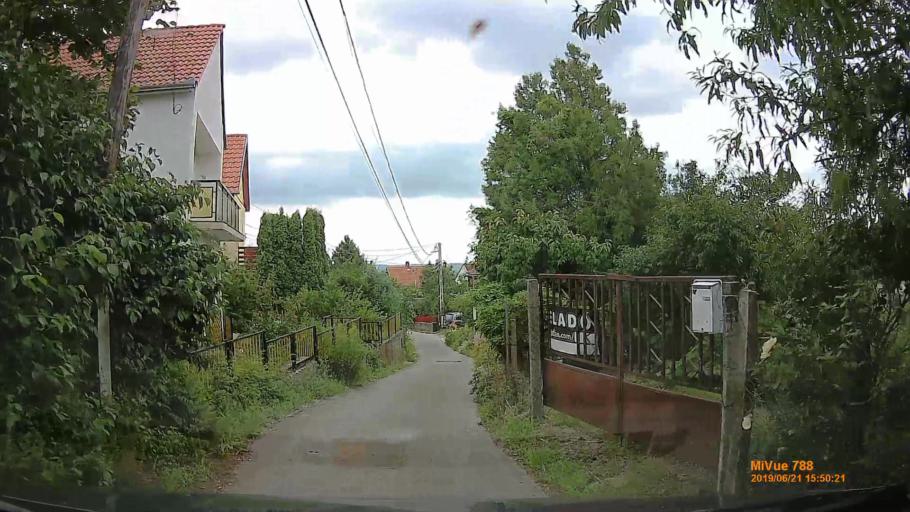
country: HU
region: Baranya
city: Pecs
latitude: 46.0891
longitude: 18.1891
